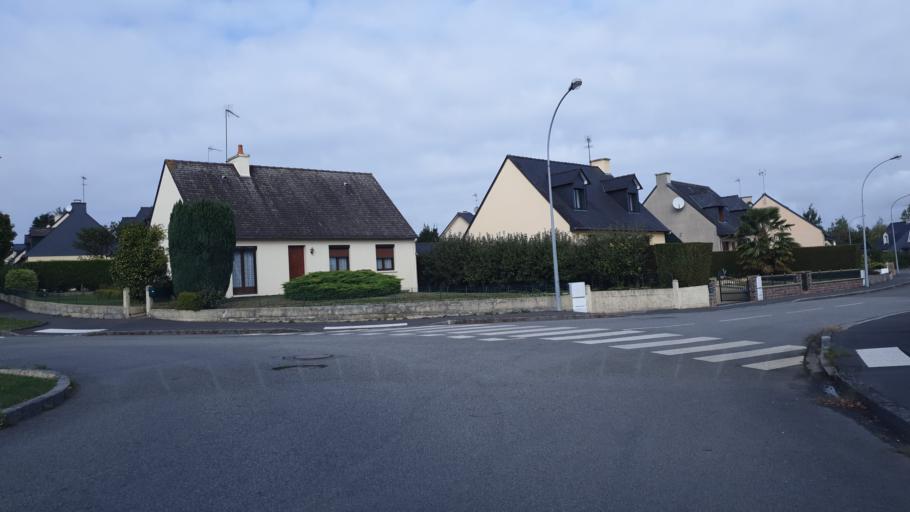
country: FR
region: Brittany
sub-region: Departement d'Ille-et-Vilaine
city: Janze
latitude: 47.9627
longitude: -1.4909
